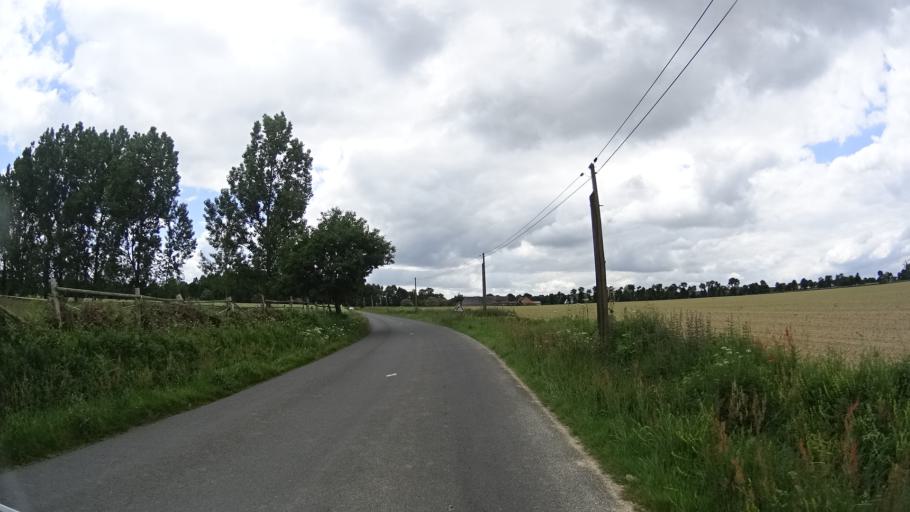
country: FR
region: Brittany
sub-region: Departement d'Ille-et-Vilaine
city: Pleumeleuc
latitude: 48.1913
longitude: -1.9105
